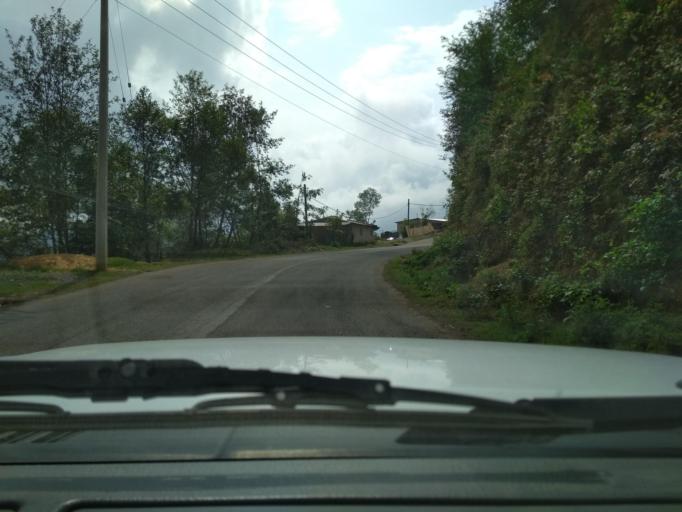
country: MX
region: Veracruz
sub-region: Camerino Z. Mendoza
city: Necoxtla
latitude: 18.7716
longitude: -97.1528
